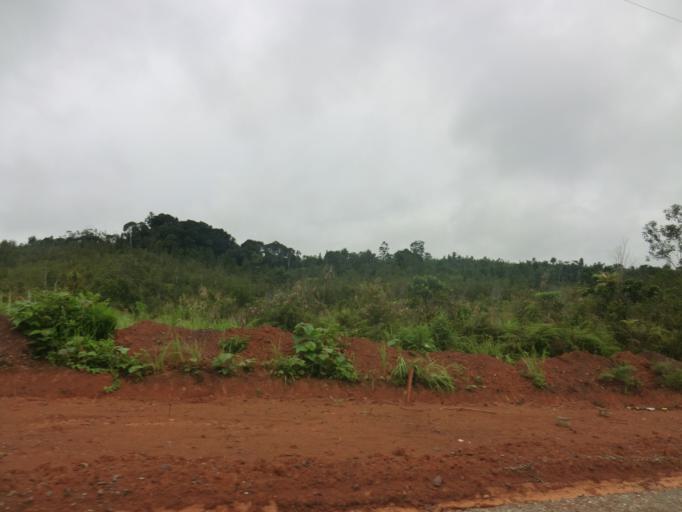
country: MY
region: Sarawak
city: Simanggang
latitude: 1.0695
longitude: 111.9614
